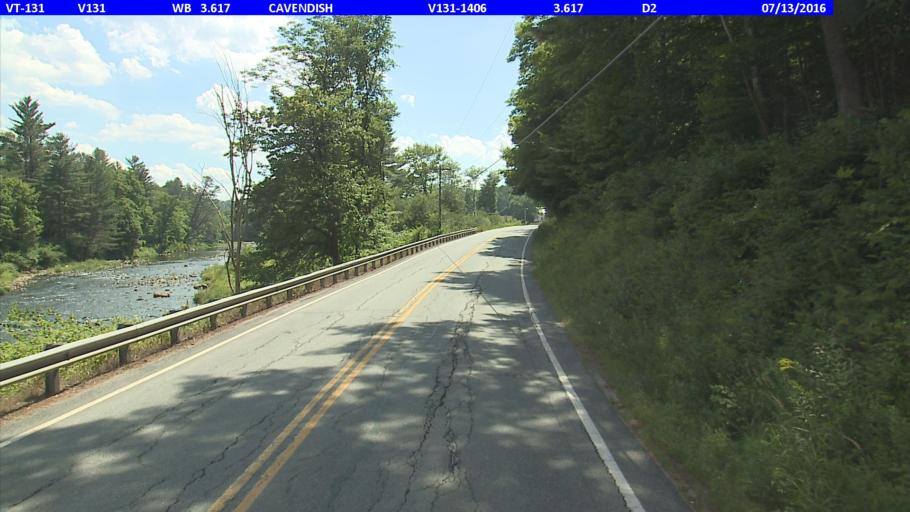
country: US
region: Vermont
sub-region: Windsor County
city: Chester
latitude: 43.3980
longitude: -72.5895
